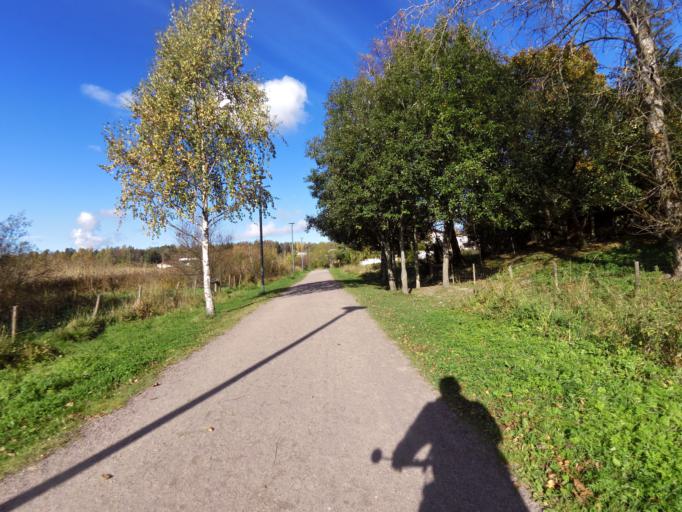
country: FI
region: Uusimaa
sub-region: Helsinki
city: Espoo
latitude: 60.1629
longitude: 24.6107
